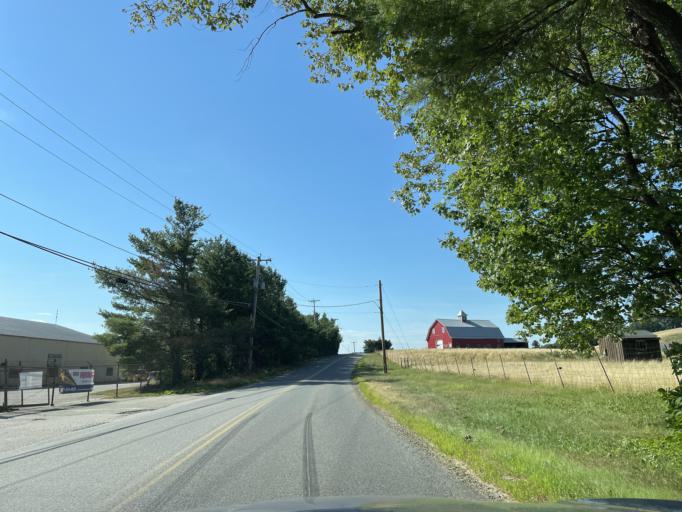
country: US
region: Massachusetts
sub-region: Worcester County
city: Charlton
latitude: 42.1571
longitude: -72.0000
